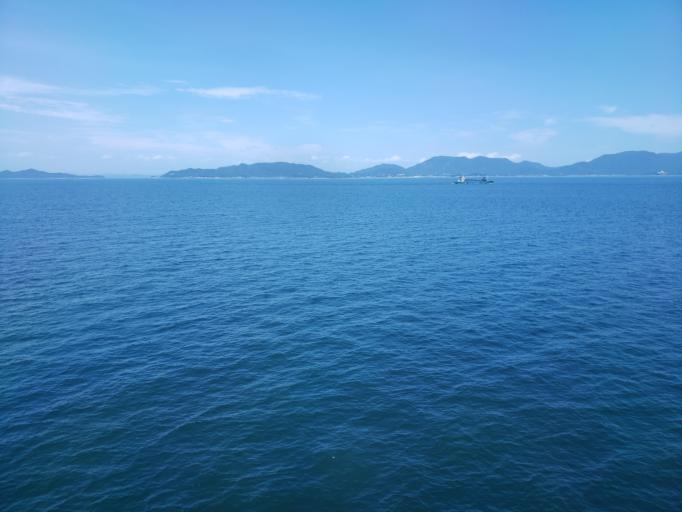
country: JP
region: Kagawa
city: Tonosho
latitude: 34.4063
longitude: 134.1726
